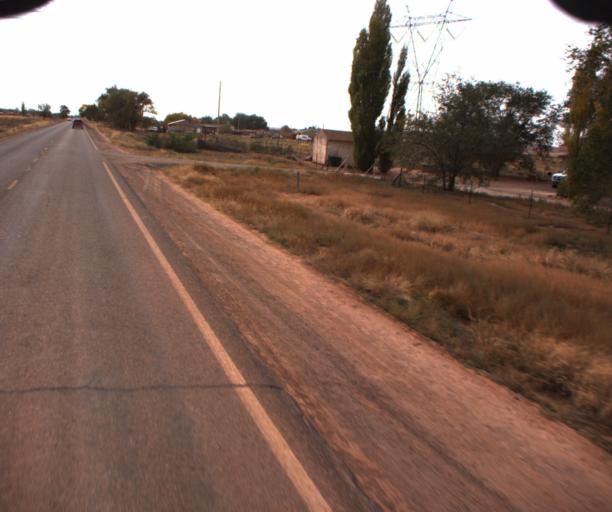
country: US
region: Arizona
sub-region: Apache County
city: Chinle
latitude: 36.2439
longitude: -109.6029
